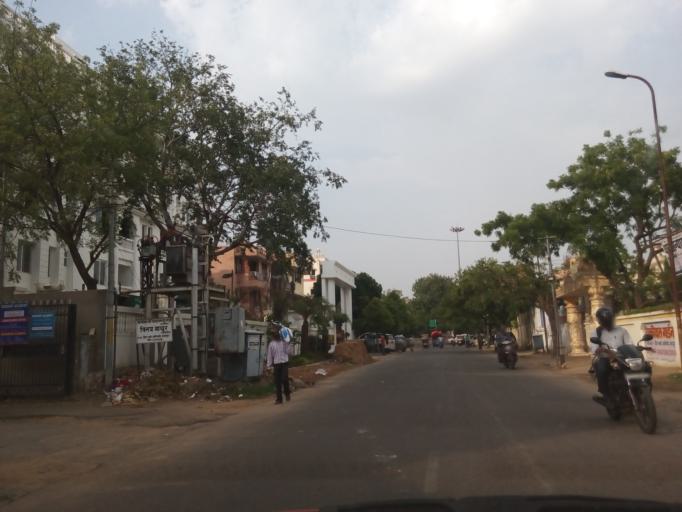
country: IN
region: Rajasthan
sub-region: Jaipur
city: Jaipur
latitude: 26.9279
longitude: 75.7965
